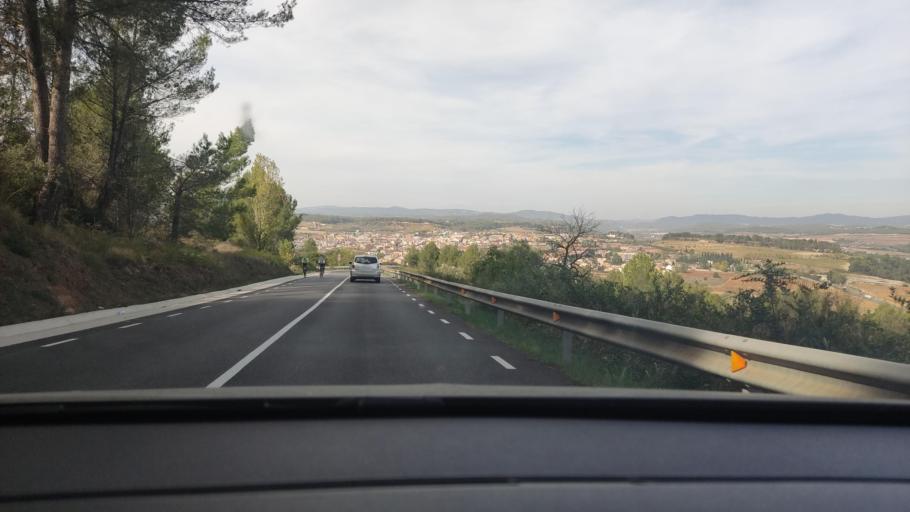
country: ES
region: Catalonia
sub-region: Provincia de Barcelona
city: Sant Sadurni d'Anoia
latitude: 41.4166
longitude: 1.8024
